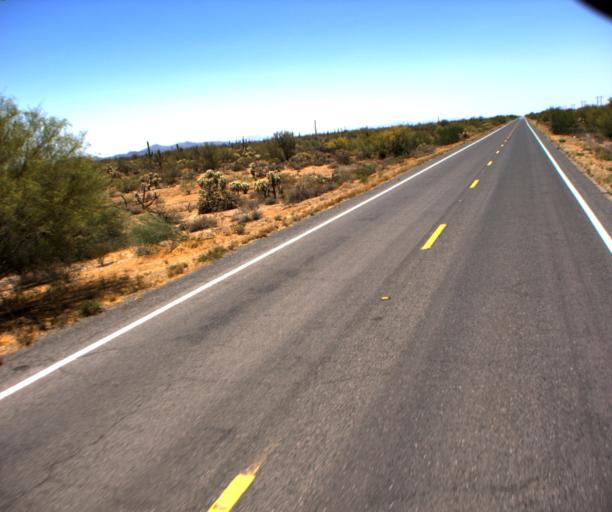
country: US
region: Arizona
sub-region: Pinal County
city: Florence
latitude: 32.7945
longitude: -111.1771
